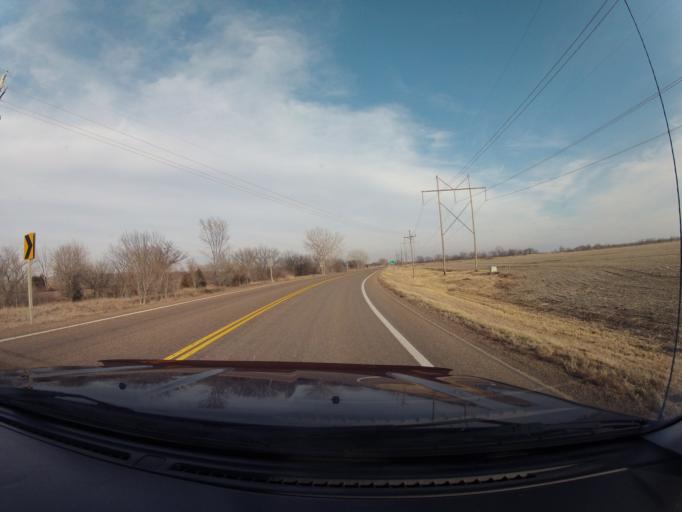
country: US
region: Kansas
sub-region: Pottawatomie County
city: Saint Marys
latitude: 39.2163
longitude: -96.1729
